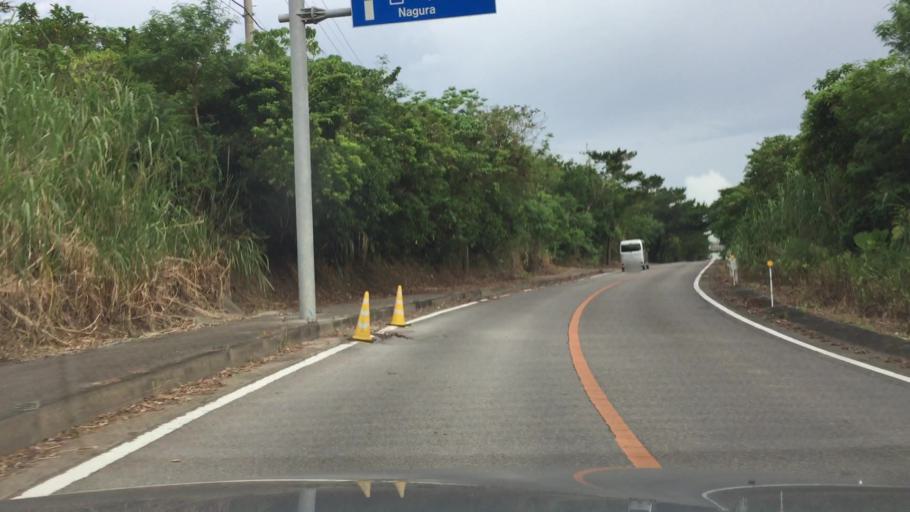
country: JP
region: Okinawa
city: Ishigaki
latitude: 24.4090
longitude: 124.1447
